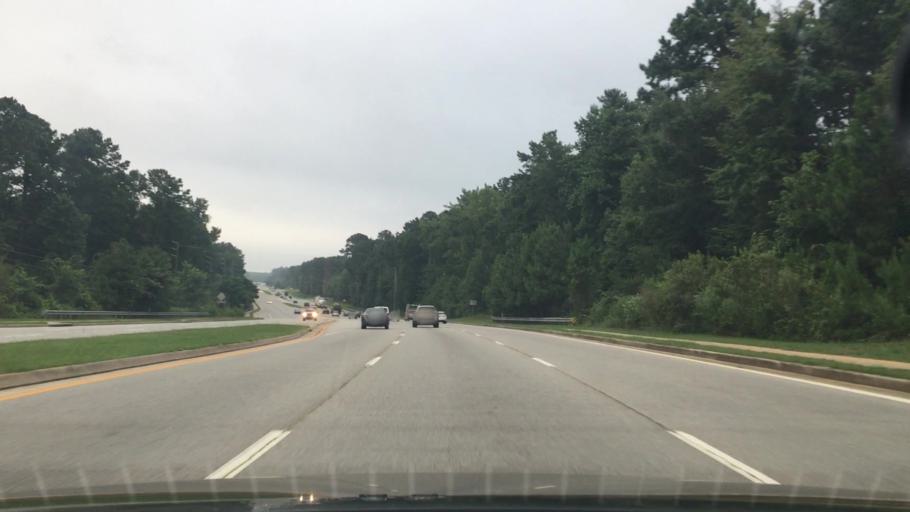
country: US
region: Georgia
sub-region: Fayette County
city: Peachtree City
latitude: 33.3812
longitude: -84.5770
